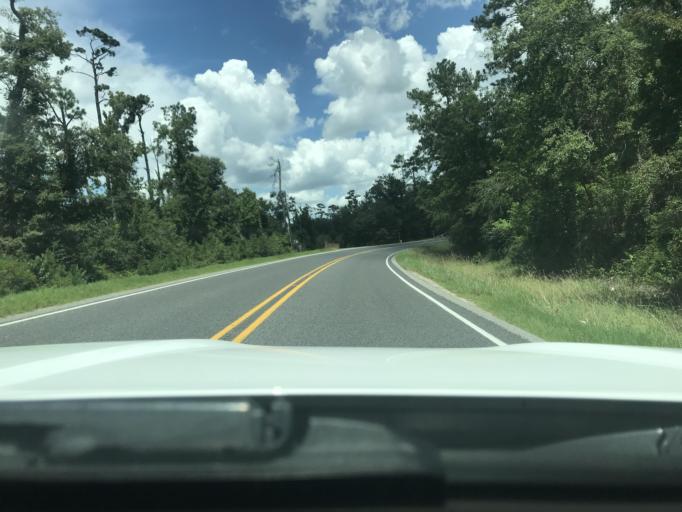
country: US
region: Louisiana
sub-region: Calcasieu Parish
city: Moss Bluff
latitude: 30.2845
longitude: -93.1678
